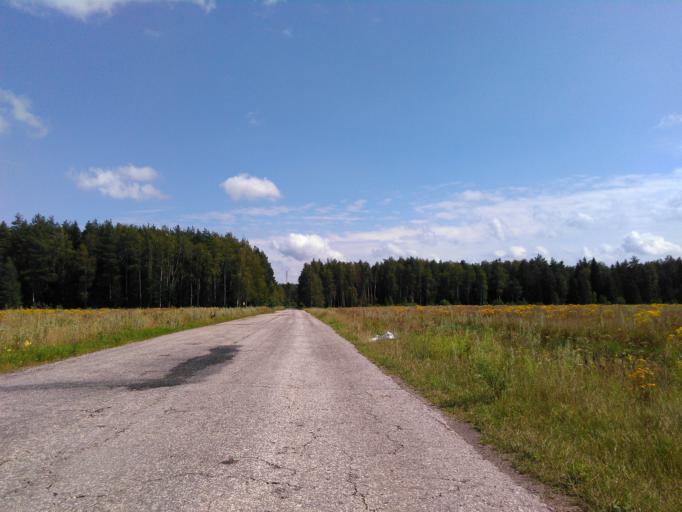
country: RU
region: Vladimir
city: Krasnyy Oktyabr'
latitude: 56.0242
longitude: 38.7806
